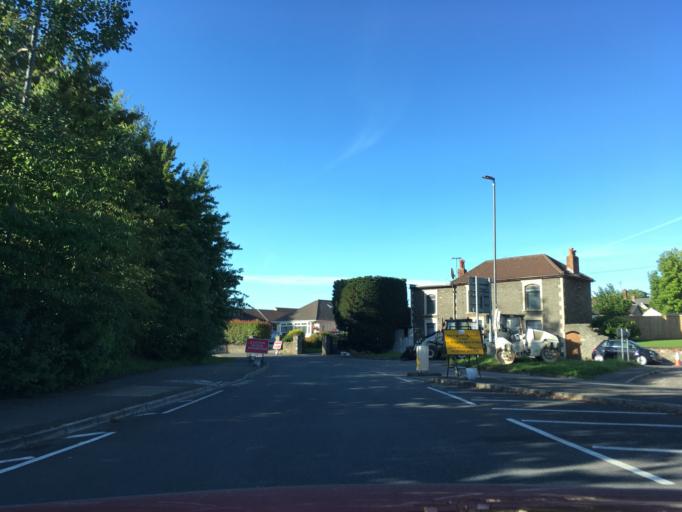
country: GB
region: England
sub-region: South Gloucestershire
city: Kingswood
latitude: 51.4410
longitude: -2.4973
